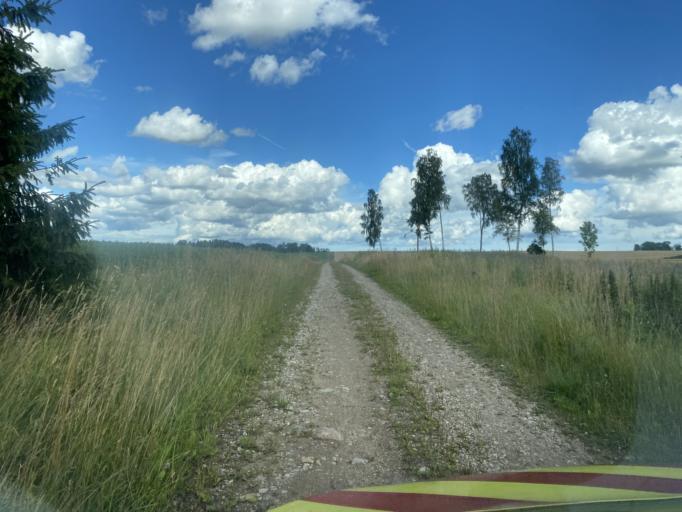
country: EE
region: Viljandimaa
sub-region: Viljandi linn
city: Viljandi
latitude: 58.2889
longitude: 25.5975
